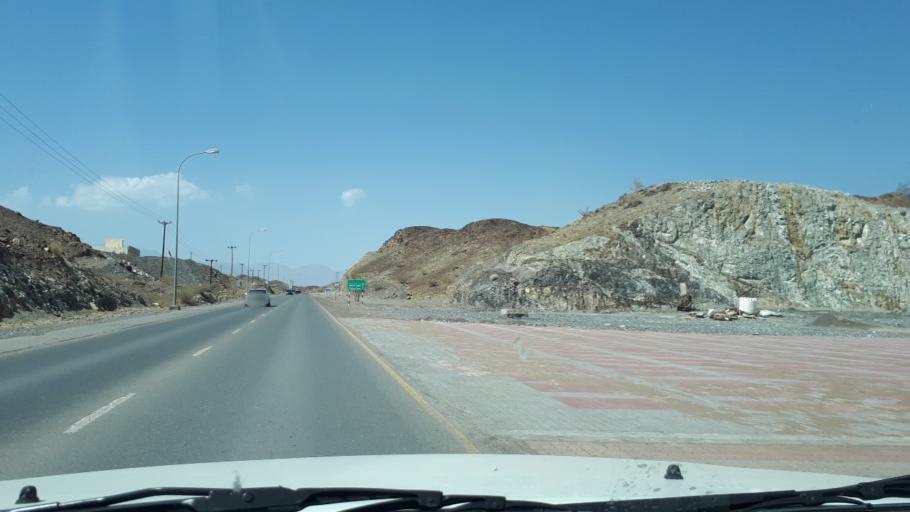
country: OM
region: Muhafazat ad Dakhiliyah
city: Bahla'
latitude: 22.9522
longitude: 57.2869
